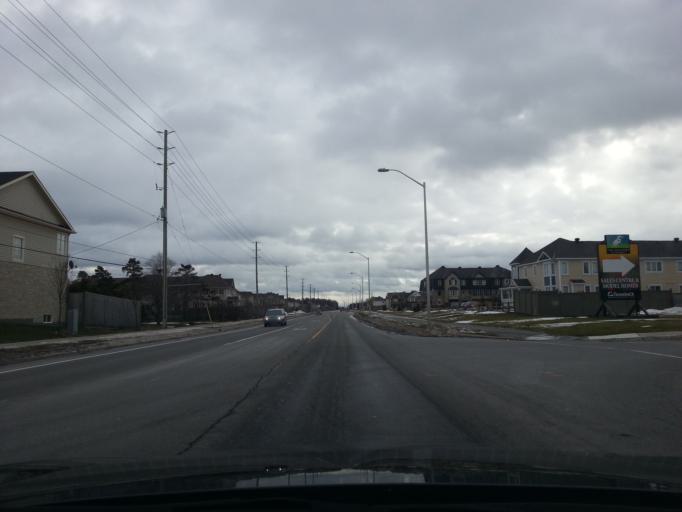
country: CA
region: Ontario
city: Bells Corners
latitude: 45.2493
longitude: -75.7336
